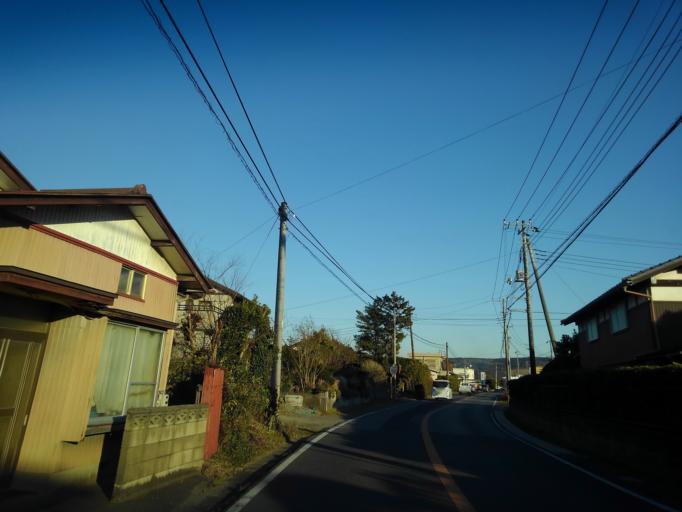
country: JP
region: Chiba
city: Kimitsu
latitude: 35.3046
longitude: 139.9670
